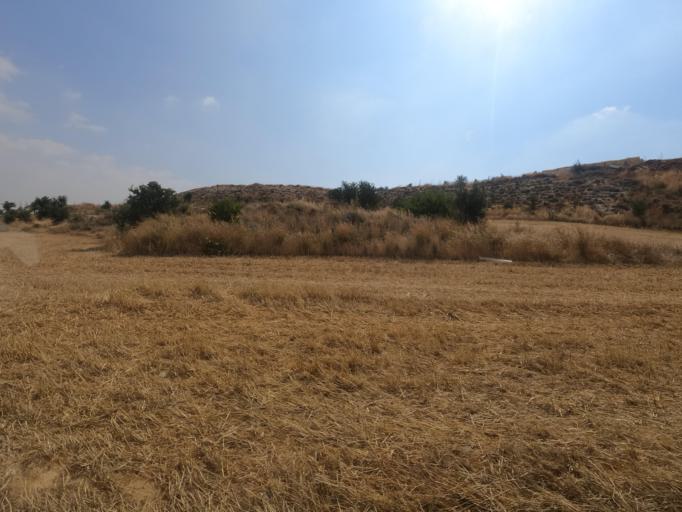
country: CY
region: Larnaka
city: Aradippou
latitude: 34.9174
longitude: 33.5407
